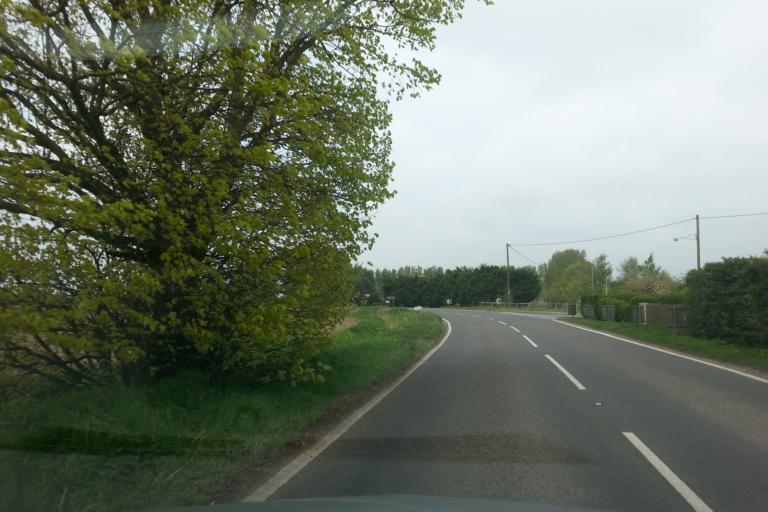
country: GB
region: England
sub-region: Norfolk
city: Outwell
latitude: 52.5697
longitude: 0.2290
